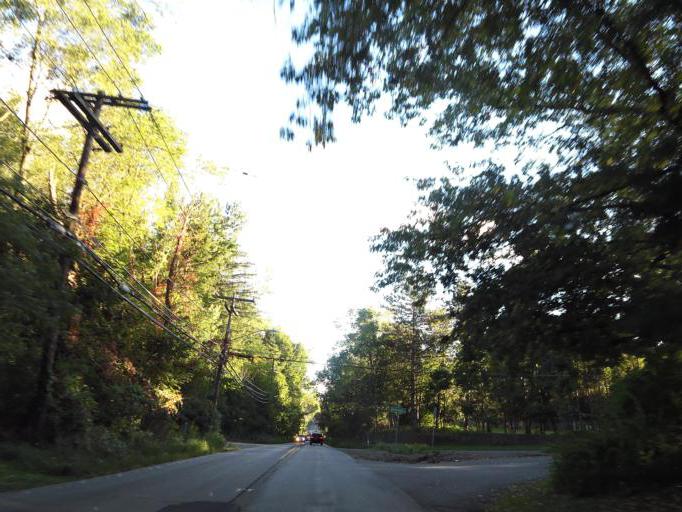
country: US
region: New York
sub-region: Erie County
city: Billington Heights
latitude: 42.7776
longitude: -78.6209
